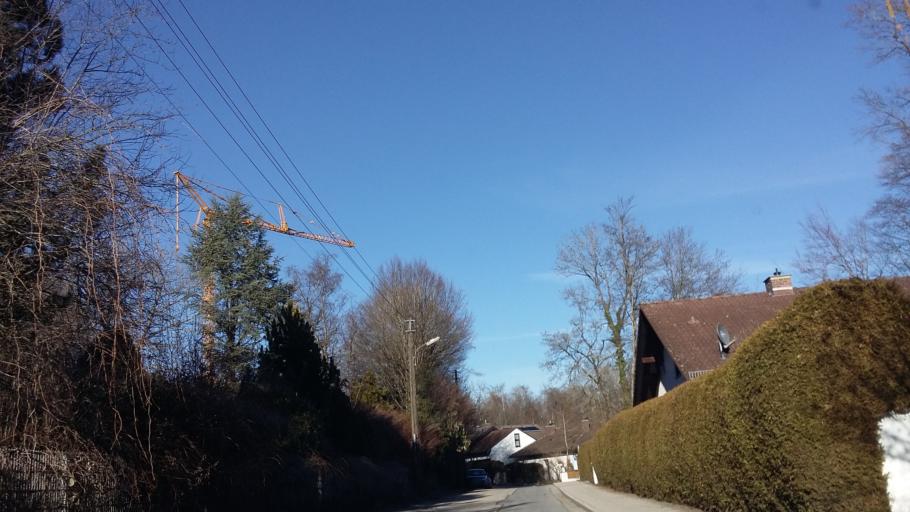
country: DE
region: Bavaria
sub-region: Upper Bavaria
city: Pocking
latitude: 47.9645
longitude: 11.3083
